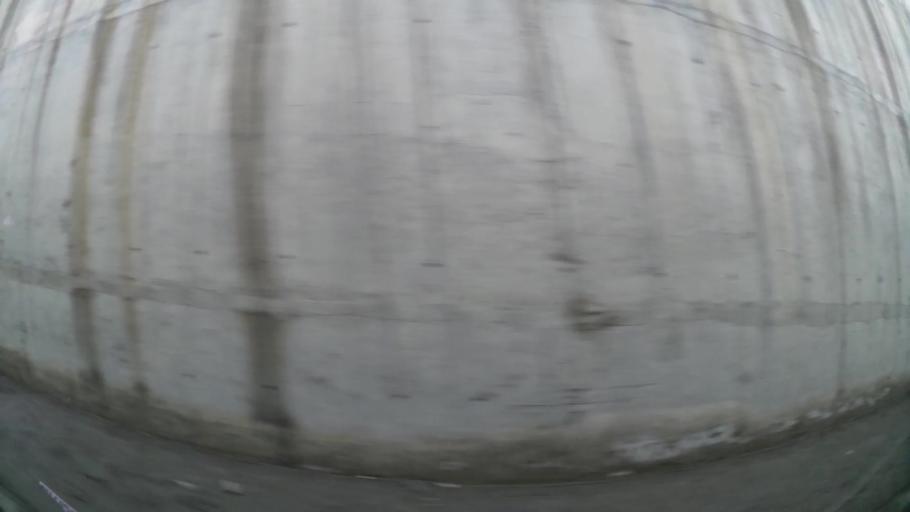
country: XK
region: Pristina
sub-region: Komuna e Prishtines
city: Pristina
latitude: 42.6457
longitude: 21.1558
